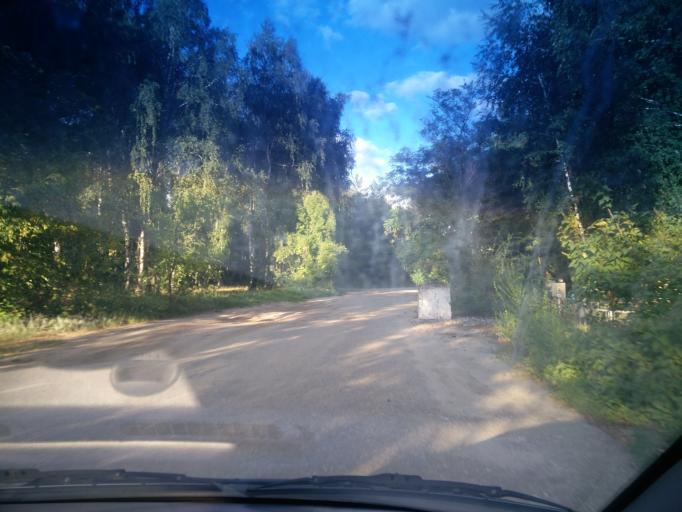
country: RU
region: Voronezj
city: Pridonskoy
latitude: 51.6738
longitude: 39.1101
